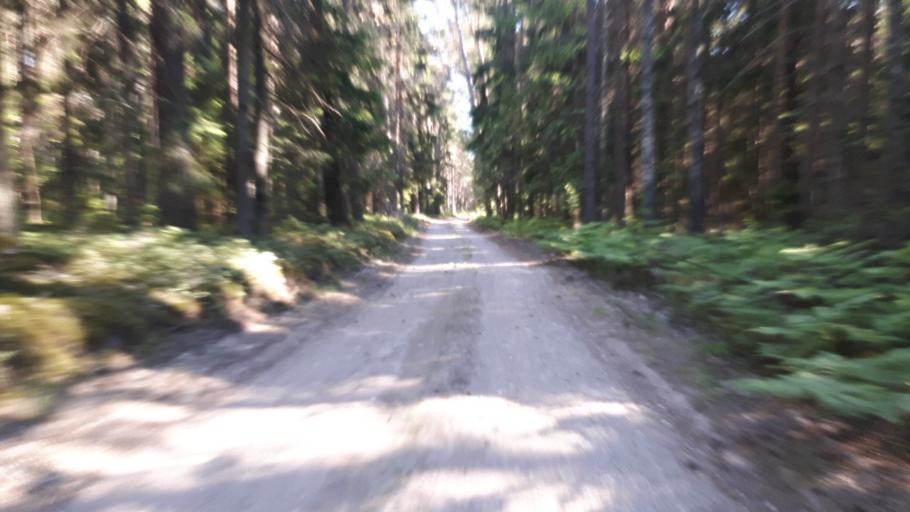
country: LV
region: Salacgrivas
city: Salacgriva
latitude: 57.7332
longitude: 24.3500
